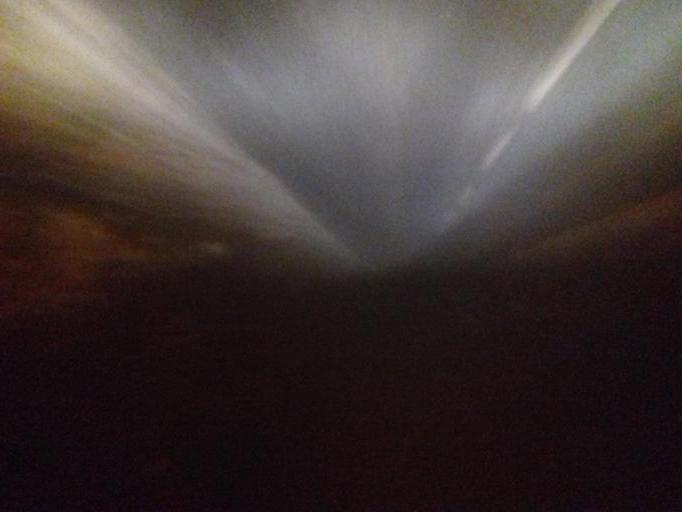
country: BA
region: Federation of Bosnia and Herzegovina
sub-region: Kanton Sarajevo
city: Sarajevo
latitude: 43.7871
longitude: 18.3613
